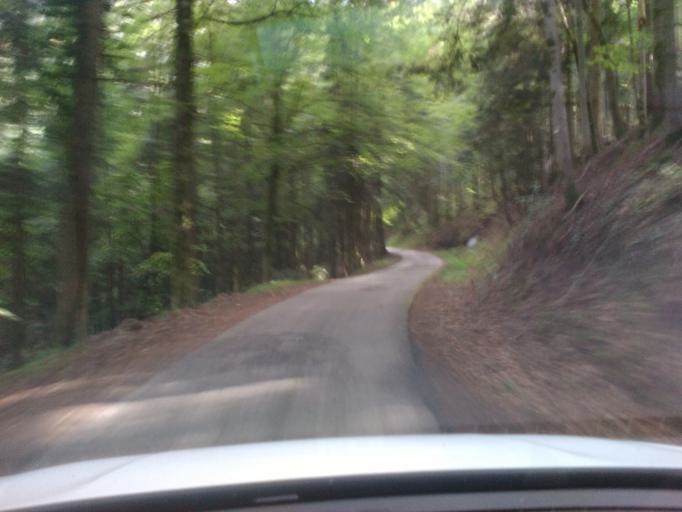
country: FR
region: Lorraine
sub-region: Departement des Vosges
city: Sainte-Marguerite
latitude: 48.3201
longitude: 7.0118
